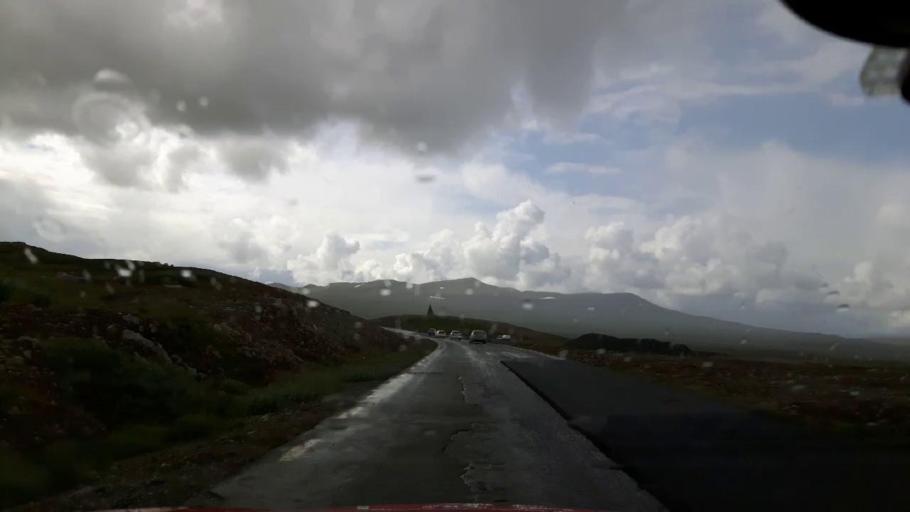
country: NO
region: Nordland
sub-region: Hattfjelldal
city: Hattfjelldal
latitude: 65.0911
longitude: 14.4610
